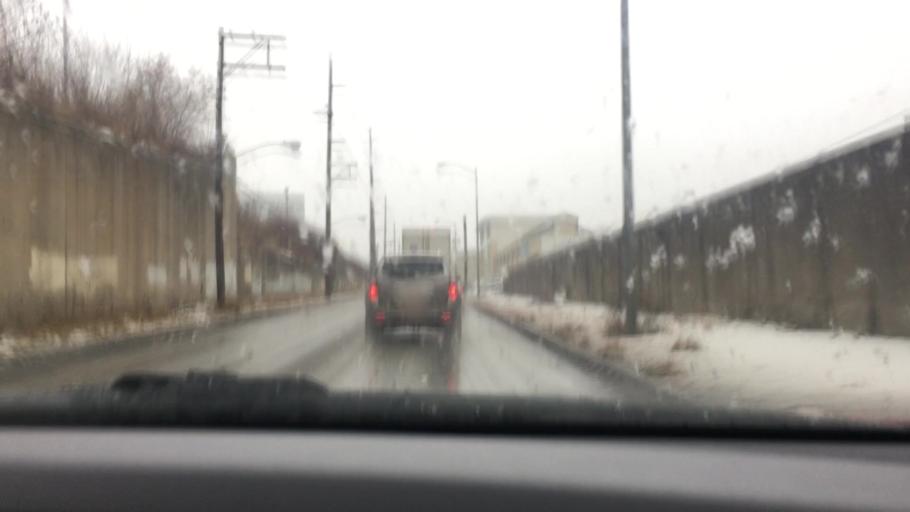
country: US
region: Pennsylvania
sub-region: Allegheny County
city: Mount Oliver
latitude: 40.4190
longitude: -79.9572
